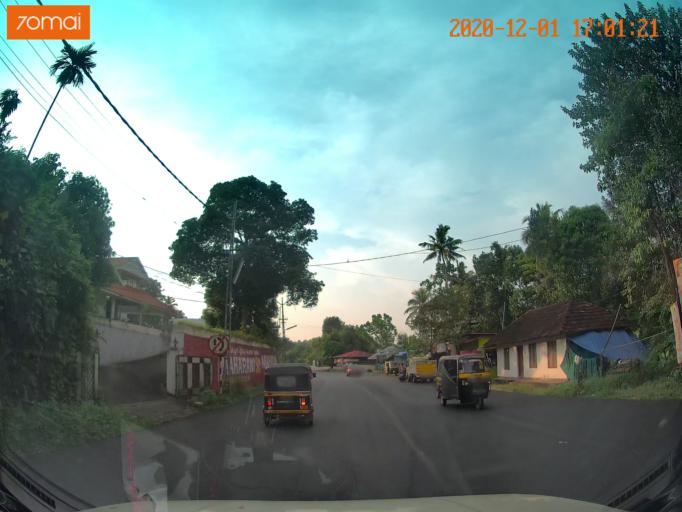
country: IN
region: Kerala
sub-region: Ernakulam
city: Muvattupula
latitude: 9.9763
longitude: 76.5925
